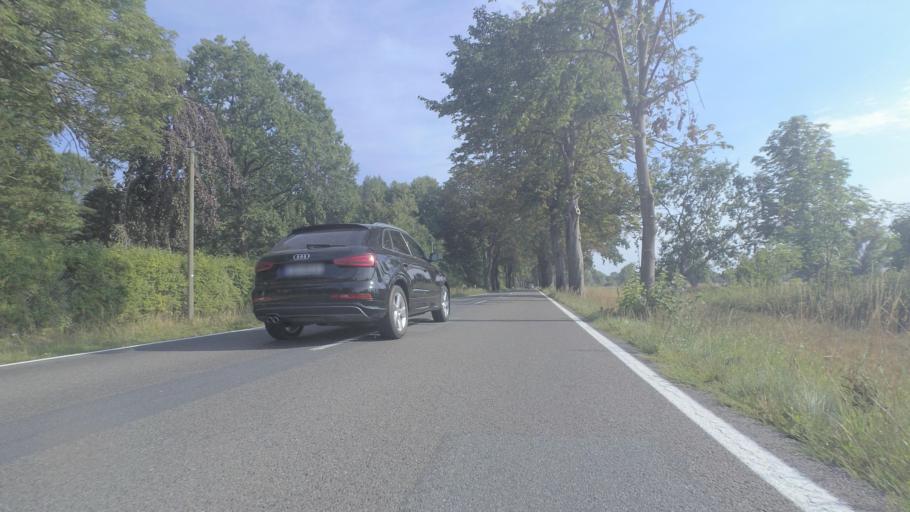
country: DE
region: Mecklenburg-Vorpommern
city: Grimmen
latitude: 54.0630
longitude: 13.1178
